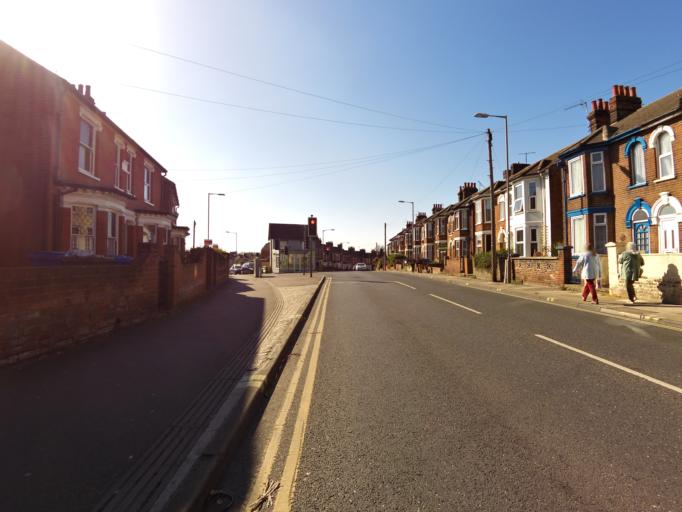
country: GB
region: England
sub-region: Suffolk
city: Ipswich
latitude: 52.0538
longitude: 1.1728
